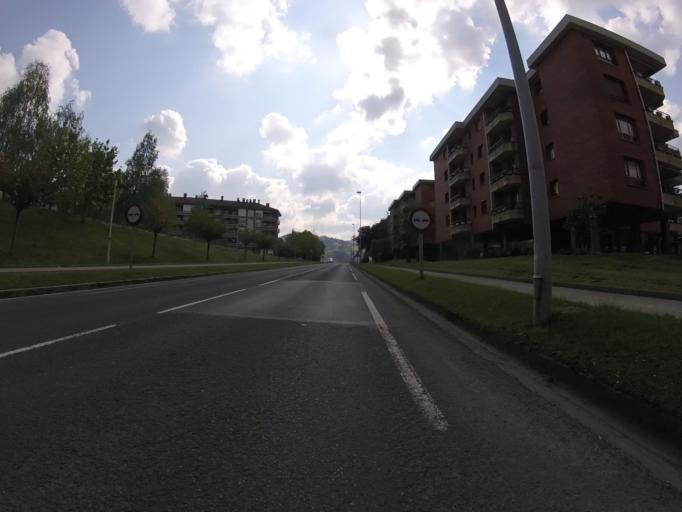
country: ES
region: Basque Country
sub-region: Provincia de Guipuzcoa
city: Azpeitia
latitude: 43.1791
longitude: -2.2665
